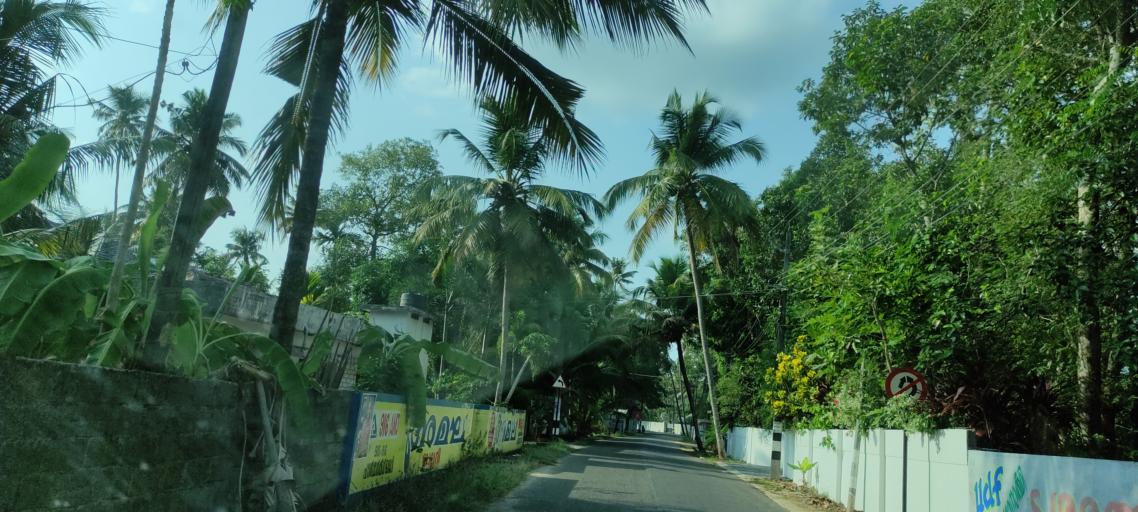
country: IN
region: Kerala
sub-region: Alappuzha
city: Vayalar
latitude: 9.7084
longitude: 76.2888
